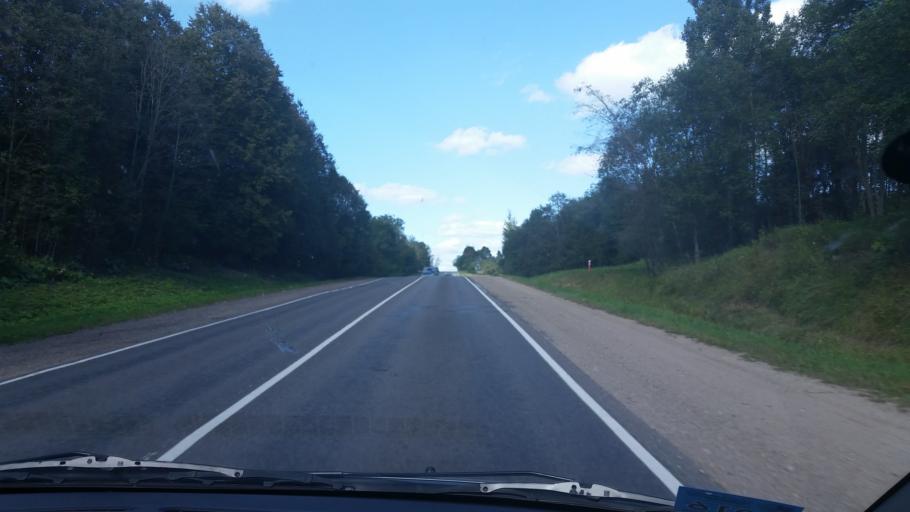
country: BY
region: Vitebsk
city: Vitebsk
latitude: 55.1074
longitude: 30.2837
